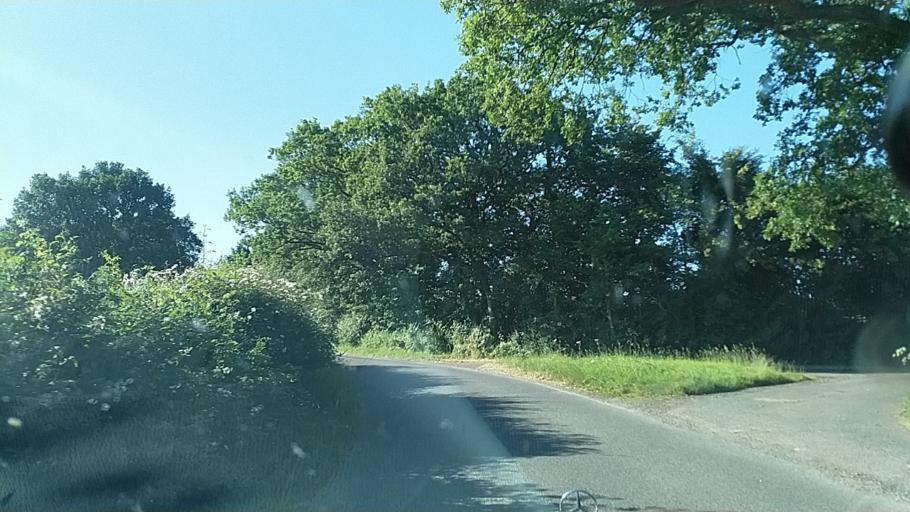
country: GB
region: England
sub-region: Warwickshire
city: Wroxall
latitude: 52.3226
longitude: -1.6448
